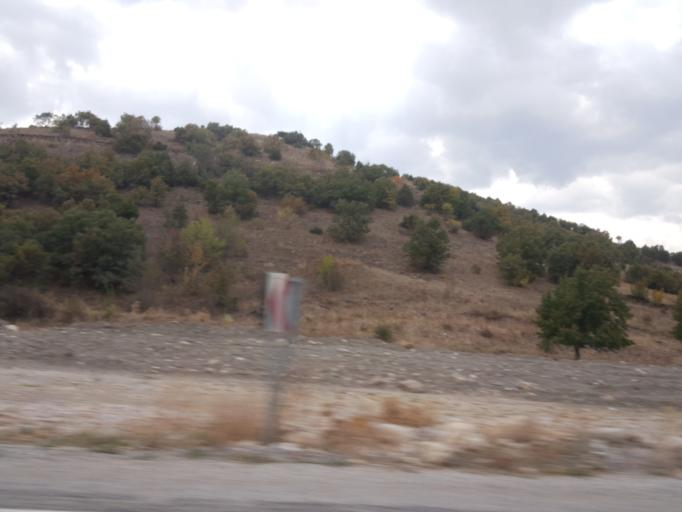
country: TR
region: Yozgat
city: Cekerek
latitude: 40.1911
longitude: 35.4162
